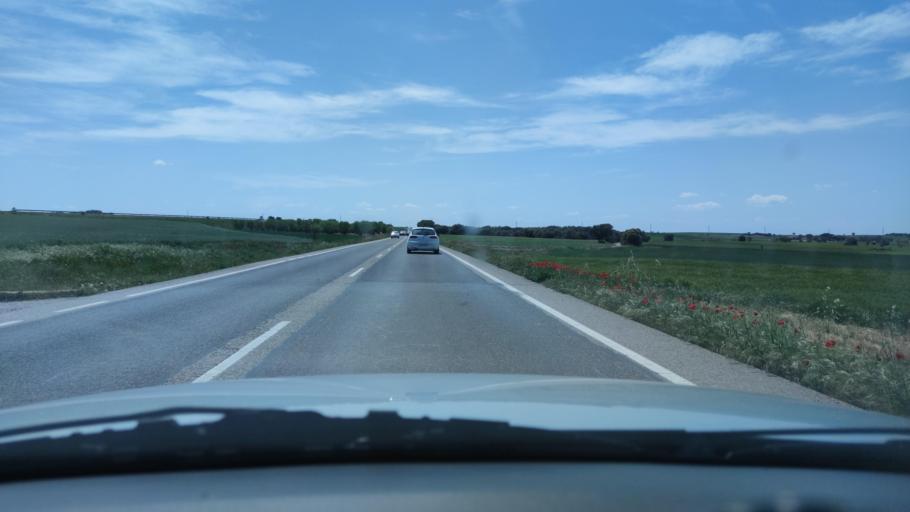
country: ES
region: Catalonia
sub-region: Provincia de Lleida
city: Mont-roig del Camp
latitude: 41.7351
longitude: 1.2151
